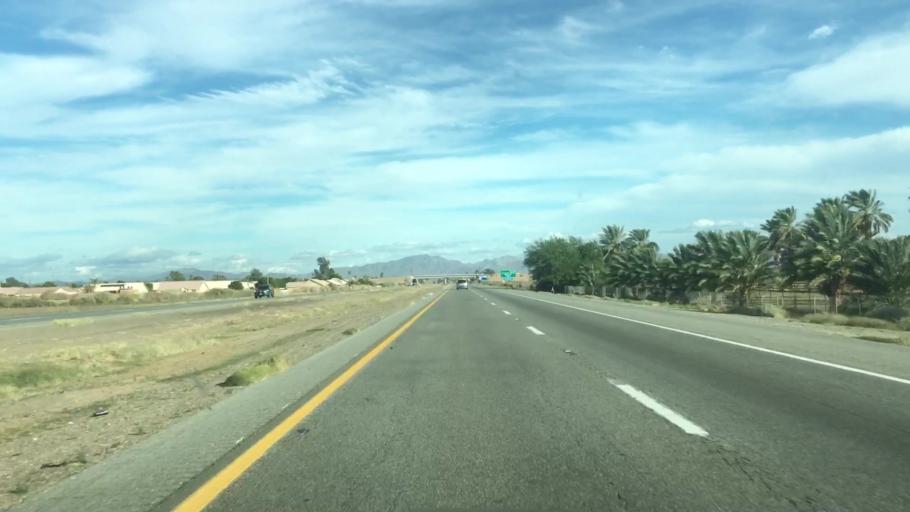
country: US
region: California
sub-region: Riverside County
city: Blythe
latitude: 33.6092
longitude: -114.6358
